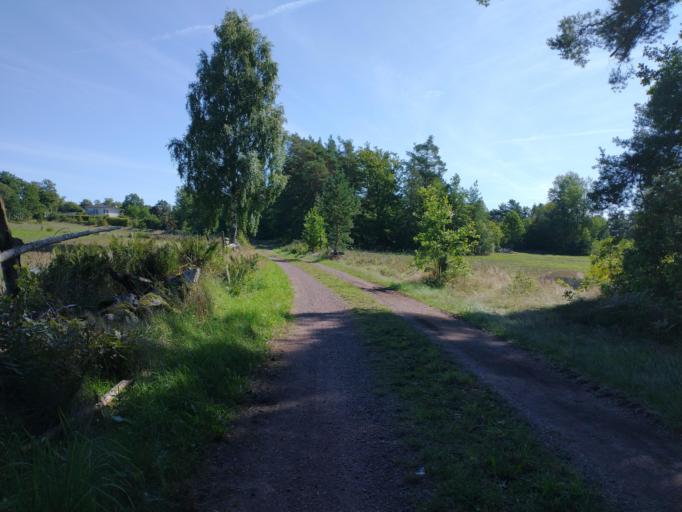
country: SE
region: Kalmar
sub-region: Kalmar Kommun
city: Lindsdal
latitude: 56.7855
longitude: 16.2856
